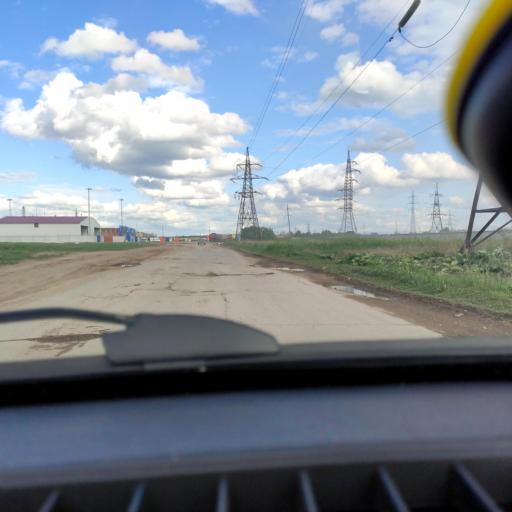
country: RU
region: Samara
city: Tol'yatti
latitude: 53.5478
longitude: 49.4676
